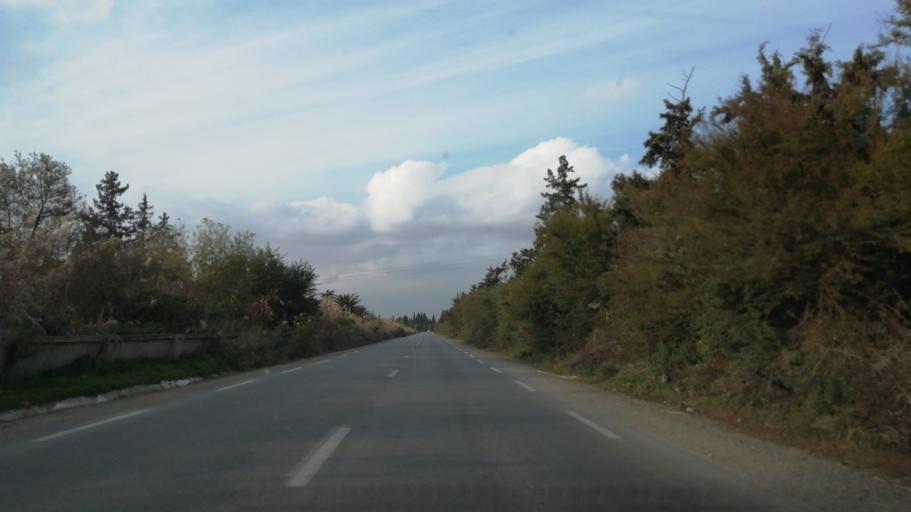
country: DZ
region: Mascara
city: Mascara
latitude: 35.6275
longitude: 0.0423
